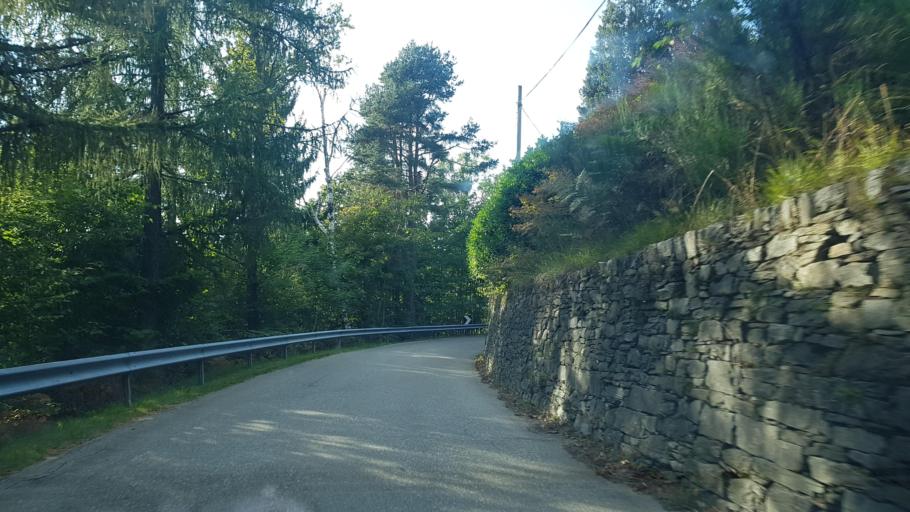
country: IT
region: Piedmont
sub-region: Provincia Verbano-Cusio-Ossola
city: Premeno
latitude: 45.9809
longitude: 8.6075
